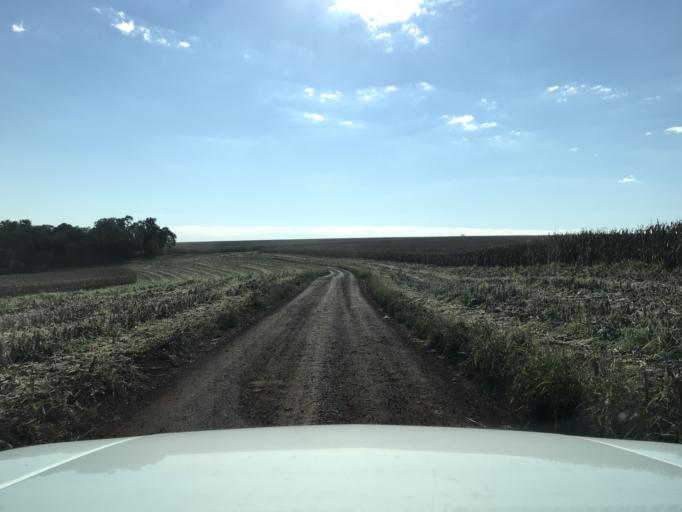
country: BR
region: Parana
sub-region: Palotina
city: Palotina
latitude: -24.2711
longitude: -53.8161
